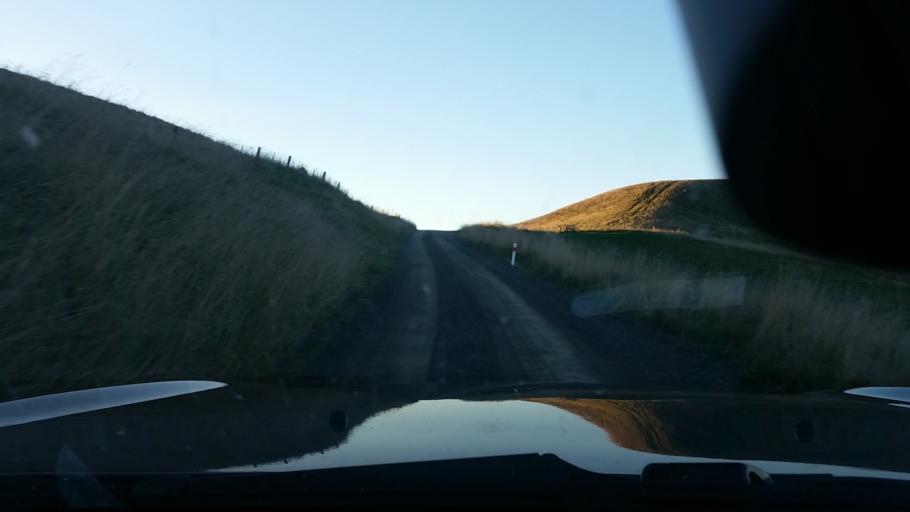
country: NZ
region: Marlborough
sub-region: Marlborough District
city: Blenheim
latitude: -41.7406
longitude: 174.0489
